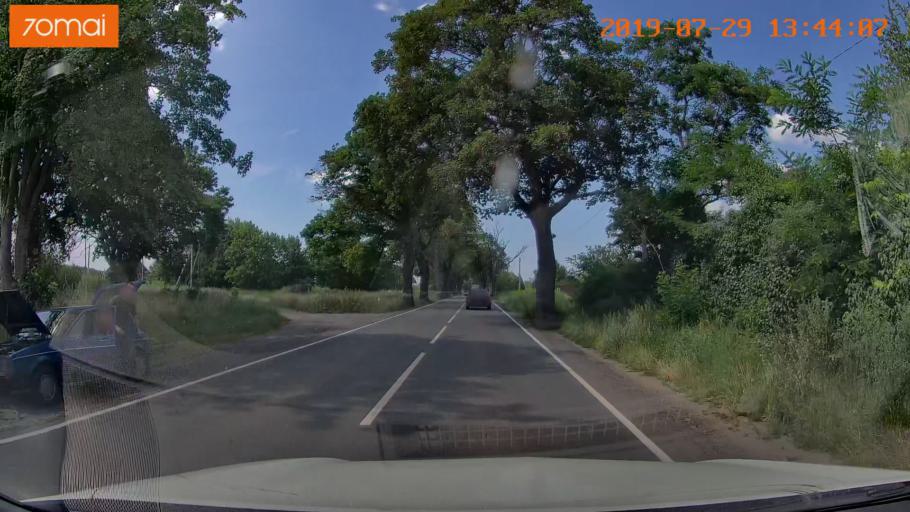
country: RU
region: Kaliningrad
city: Svetlyy
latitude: 54.7372
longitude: 20.0927
